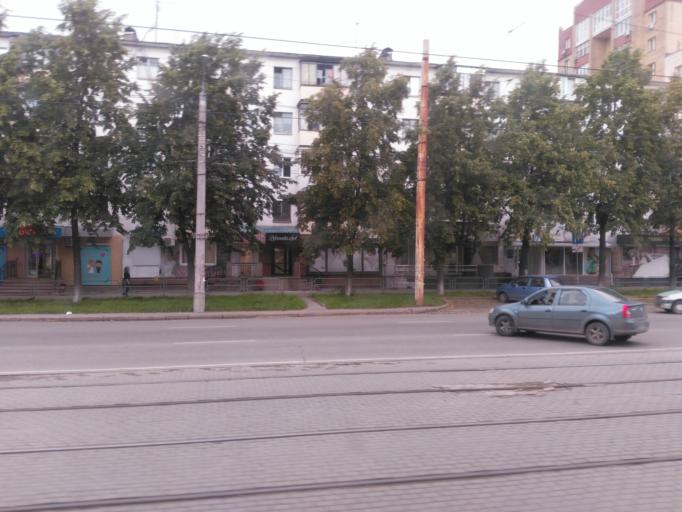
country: RU
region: Chelyabinsk
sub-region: Gorod Chelyabinsk
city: Chelyabinsk
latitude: 55.1818
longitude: 61.3989
